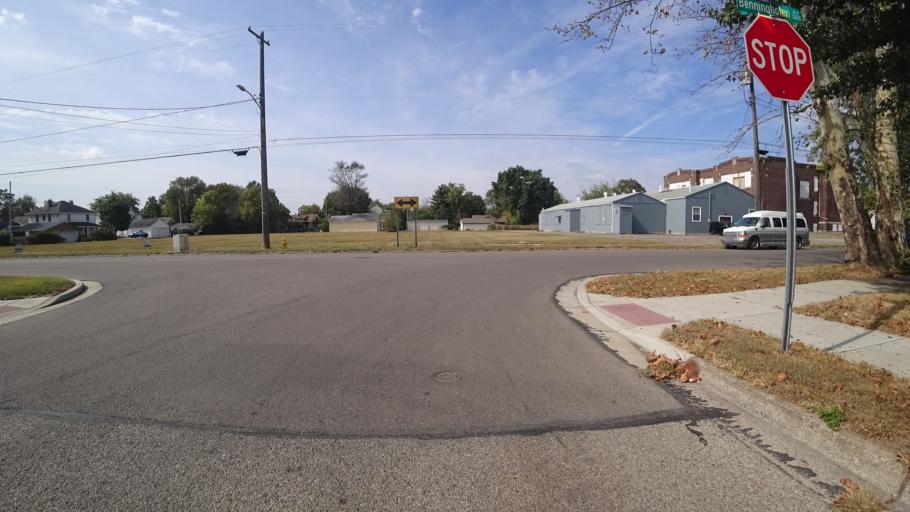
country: US
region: Ohio
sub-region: Butler County
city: Fairfield
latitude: 39.3630
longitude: -84.5560
